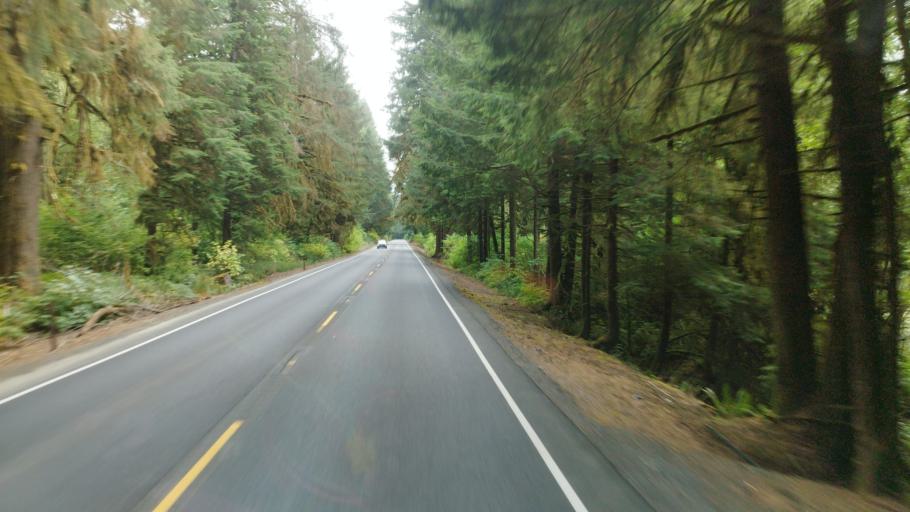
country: US
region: Oregon
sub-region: Clatsop County
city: Seaside
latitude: 45.8930
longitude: -123.6393
